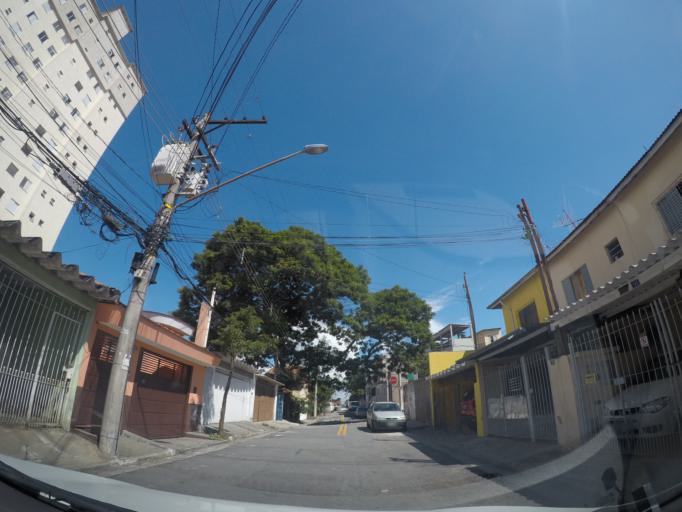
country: BR
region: Sao Paulo
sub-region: Guarulhos
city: Guarulhos
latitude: -23.4573
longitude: -46.5428
